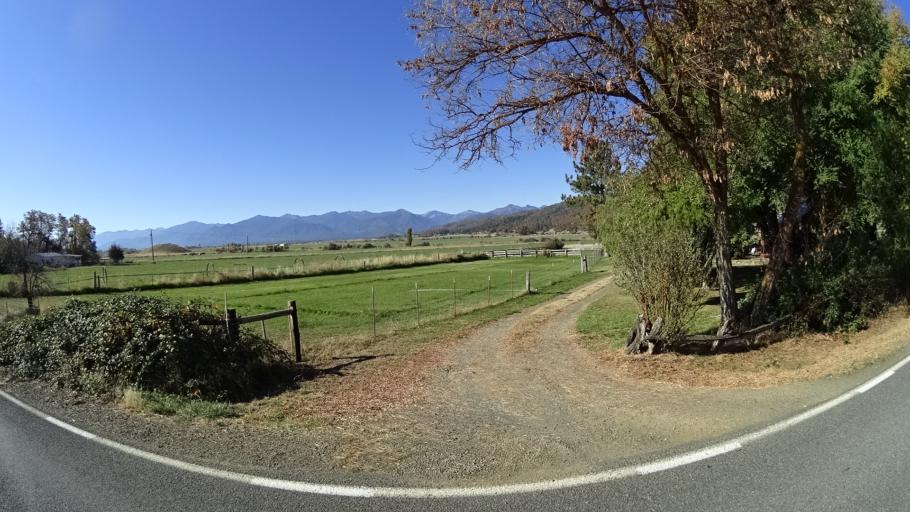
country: US
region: California
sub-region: Siskiyou County
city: Yreka
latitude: 41.5918
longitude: -122.8389
